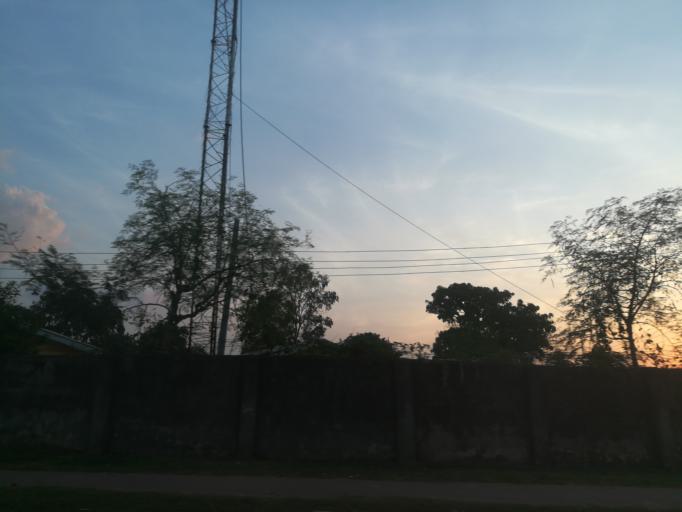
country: NG
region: Abuja Federal Capital Territory
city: Abuja
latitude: 9.0764
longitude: 7.3950
